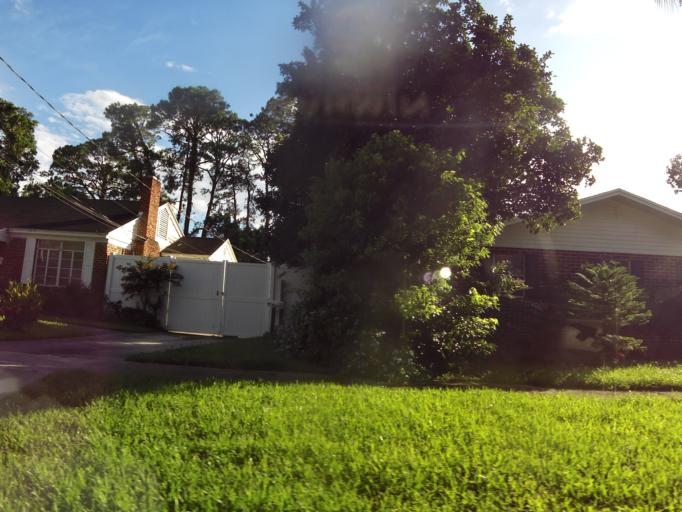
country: US
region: Florida
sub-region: Duval County
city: Jacksonville
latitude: 30.3095
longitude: -81.7185
